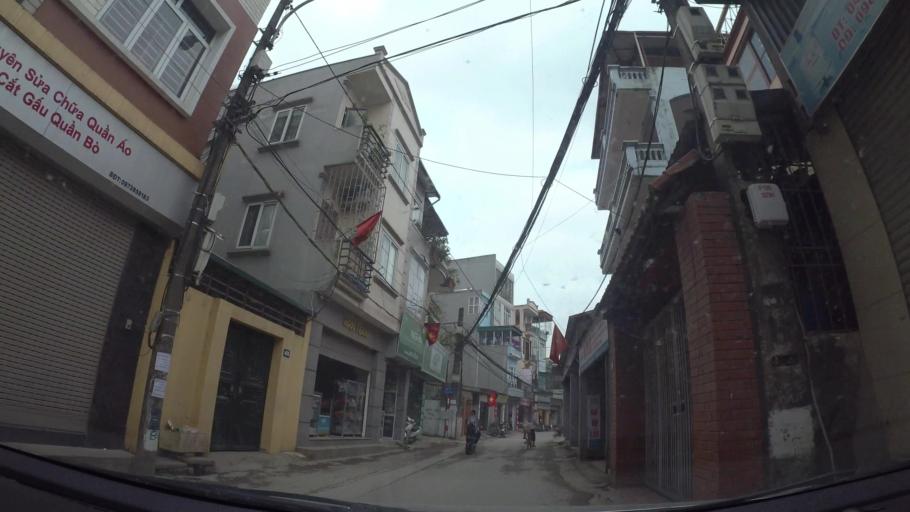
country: VN
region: Ha Noi
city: Tay Ho
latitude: 21.0735
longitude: 105.7889
